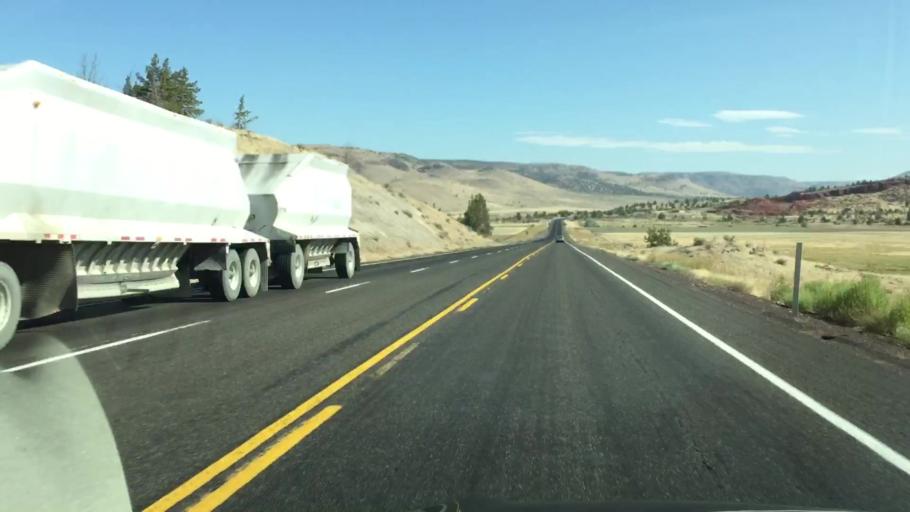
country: US
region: Oregon
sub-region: Jefferson County
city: Madras
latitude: 44.7677
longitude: -120.9713
